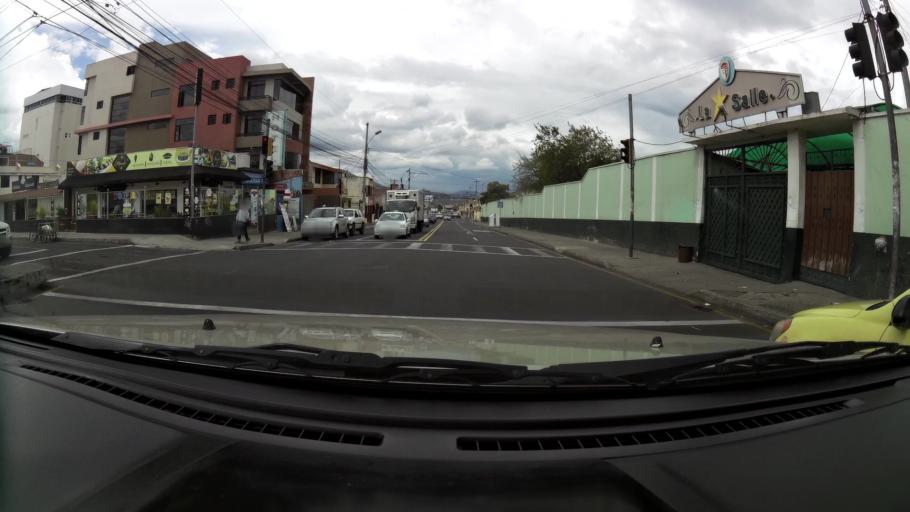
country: EC
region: Tungurahua
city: Banos
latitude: -1.3991
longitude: -78.2940
